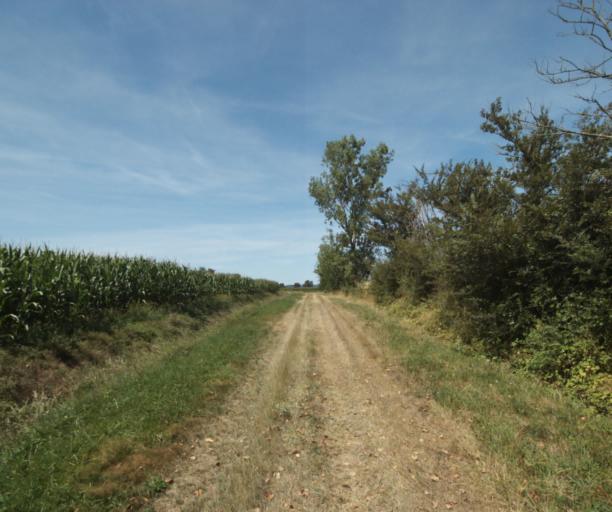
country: FR
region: Midi-Pyrenees
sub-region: Departement de la Haute-Garonne
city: Revel
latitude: 43.5029
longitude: 2.0297
